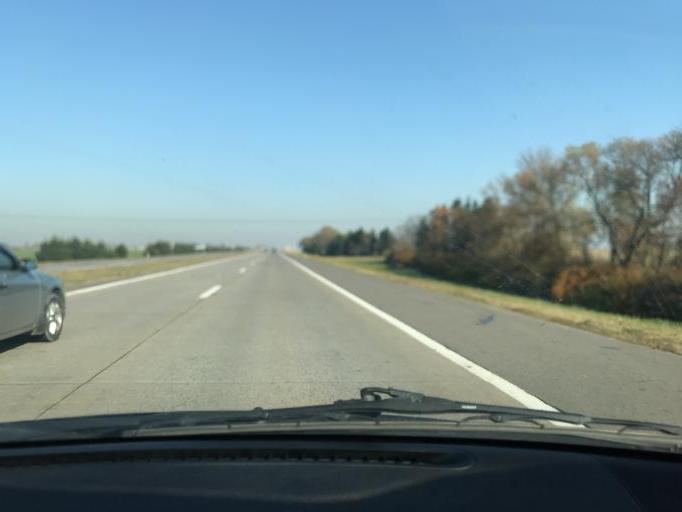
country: BY
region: Minsk
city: Samakhvalavichy
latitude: 53.6608
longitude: 27.4818
